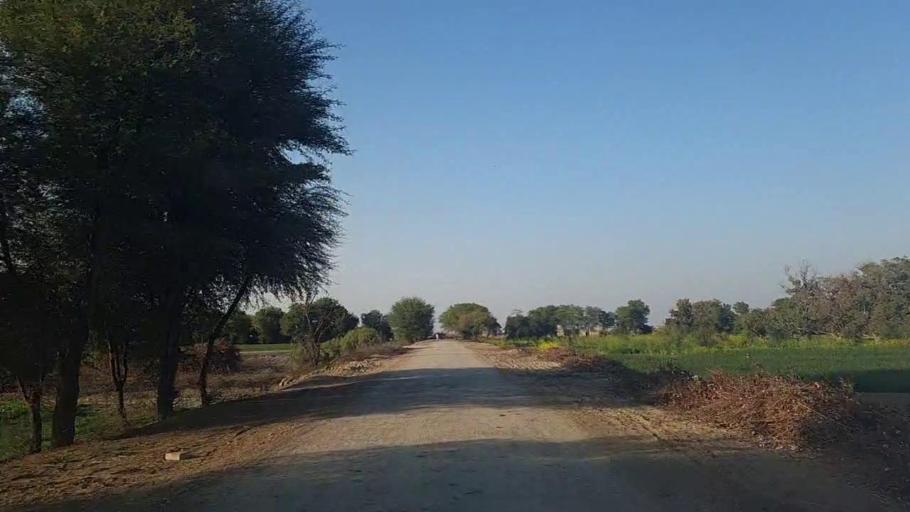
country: PK
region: Sindh
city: Jam Sahib
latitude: 26.3060
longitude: 68.6703
